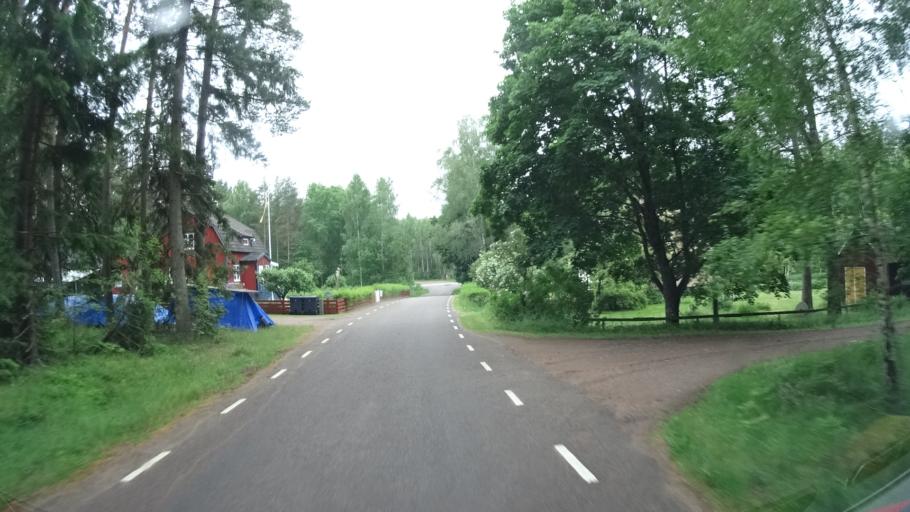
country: SE
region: Kalmar
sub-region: Vimmerby Kommun
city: Sodra Vi
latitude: 57.6870
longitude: 15.6835
